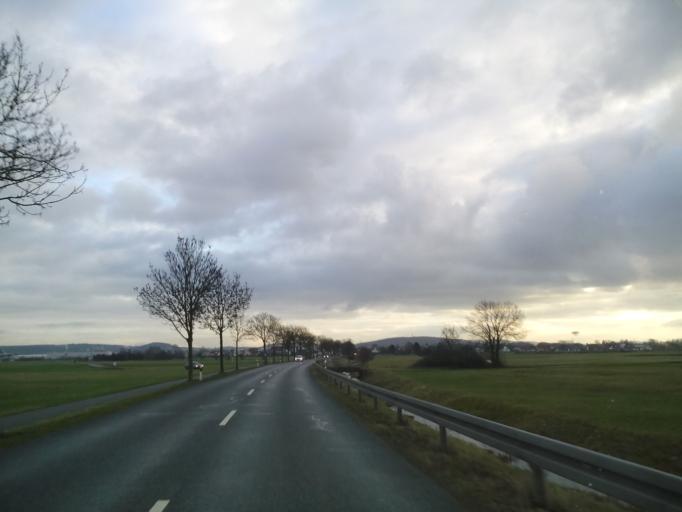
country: DE
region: Bavaria
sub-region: Upper Franconia
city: Michelau
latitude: 50.1629
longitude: 11.0865
